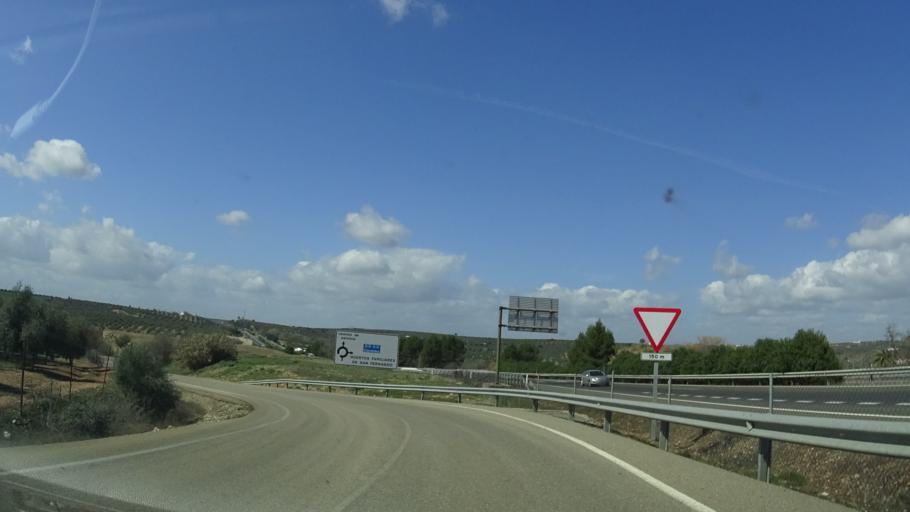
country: ES
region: Andalusia
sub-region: Province of Cordoba
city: Montoro
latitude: 38.0046
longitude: -4.3476
